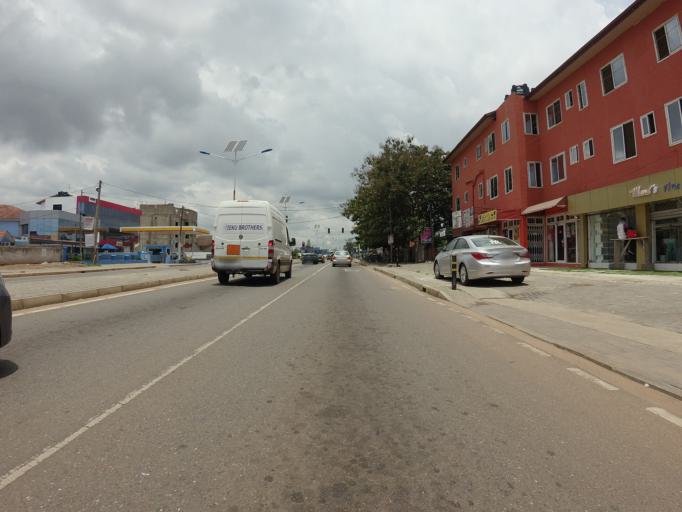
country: GH
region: Greater Accra
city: Medina Estates
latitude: 5.6500
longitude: -0.1505
